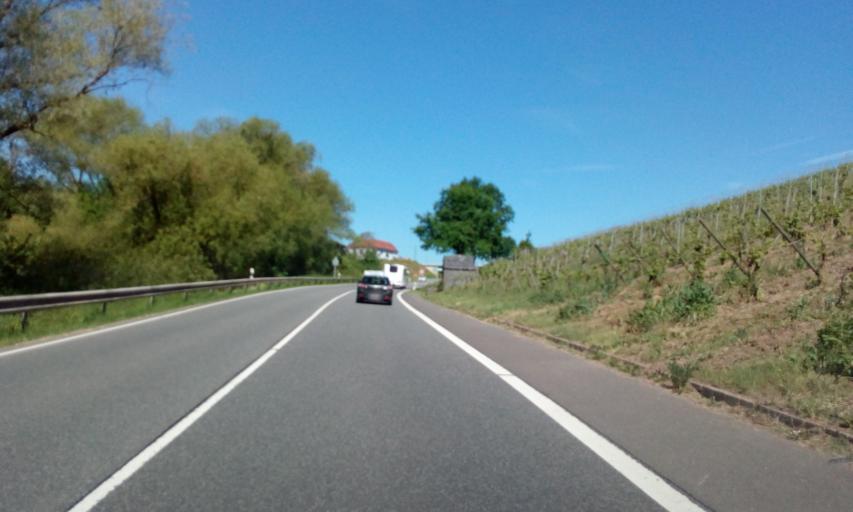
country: DE
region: Rheinland-Pfalz
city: Bekond
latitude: 49.8489
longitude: 6.8139
